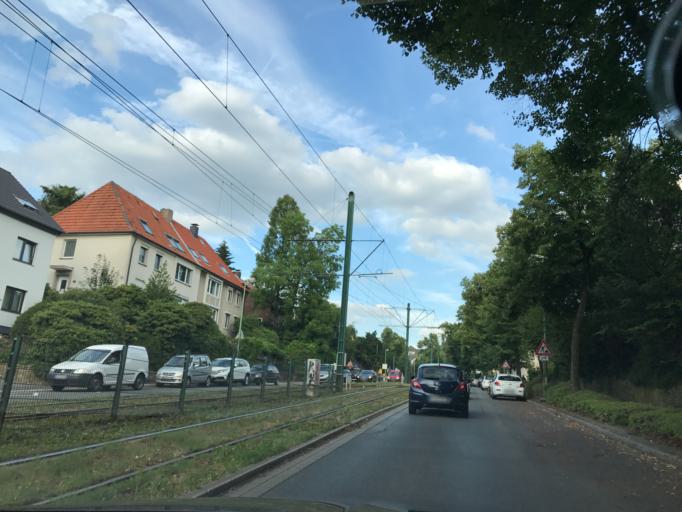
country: DE
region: North Rhine-Westphalia
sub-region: Regierungsbezirk Dusseldorf
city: Essen
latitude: 51.4362
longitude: 6.9819
